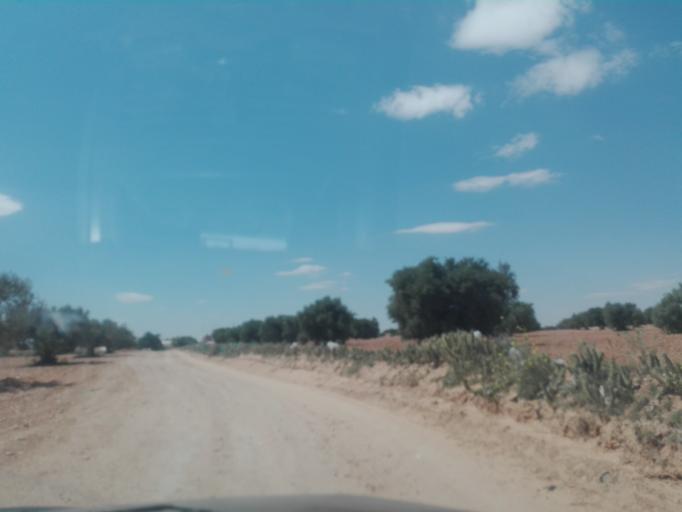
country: TN
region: Safaqis
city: Sfax
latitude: 34.6499
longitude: 10.5939
